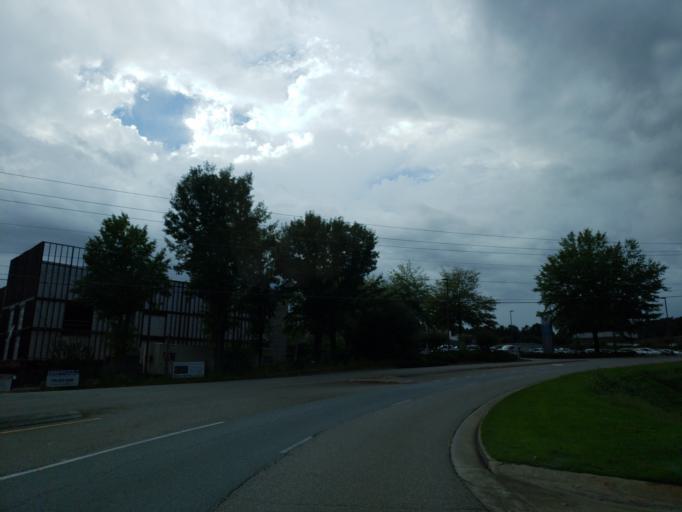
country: US
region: Georgia
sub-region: Cherokee County
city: Woodstock
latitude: 34.1034
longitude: -84.5280
